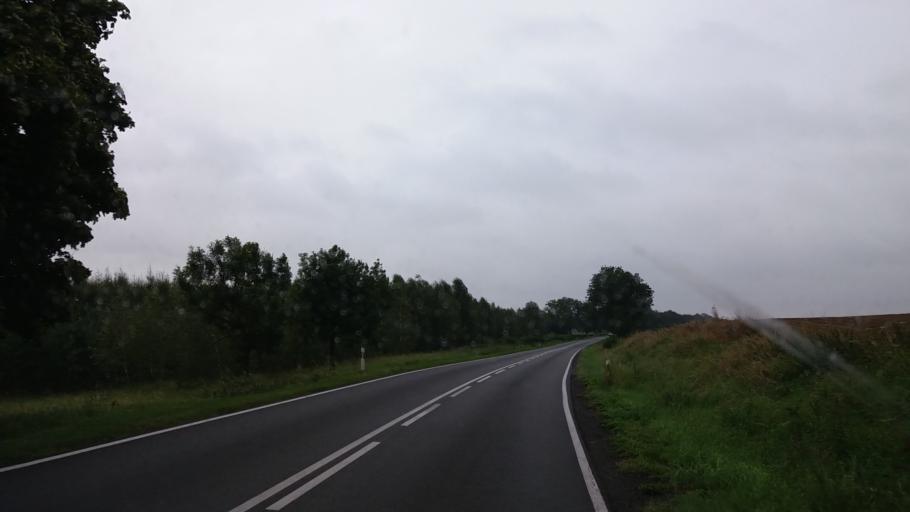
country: PL
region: West Pomeranian Voivodeship
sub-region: Powiat choszczenski
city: Pelczyce
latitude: 53.0624
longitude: 15.3018
